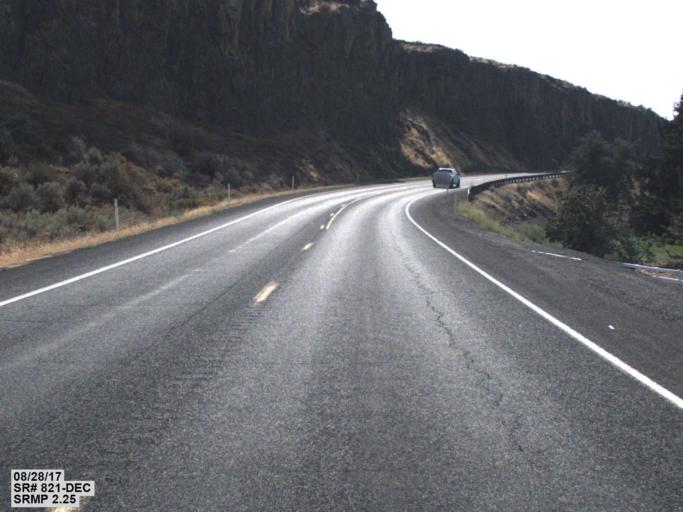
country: US
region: Washington
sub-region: Yakima County
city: Selah
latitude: 46.7066
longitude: -120.4695
